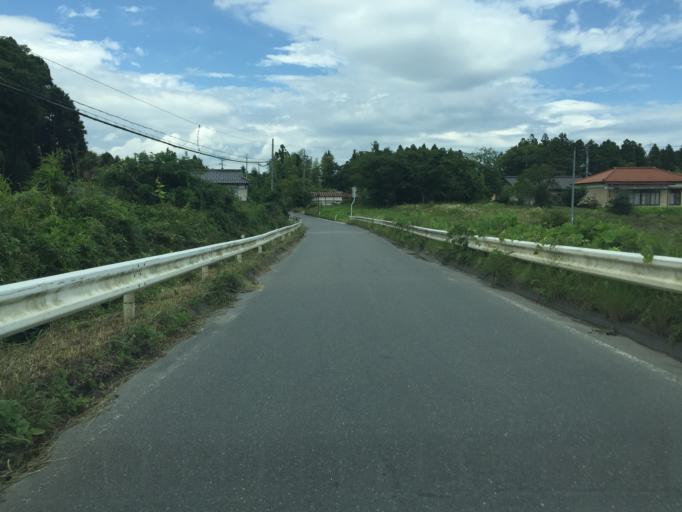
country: JP
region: Miyagi
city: Marumori
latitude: 37.7635
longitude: 140.9158
